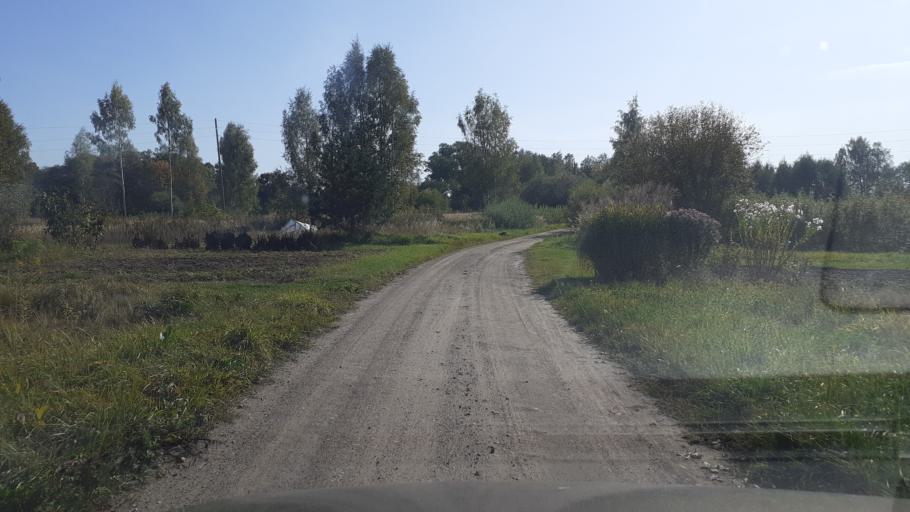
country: LV
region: Kuldigas Rajons
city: Kuldiga
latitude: 56.9501
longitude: 21.9947
